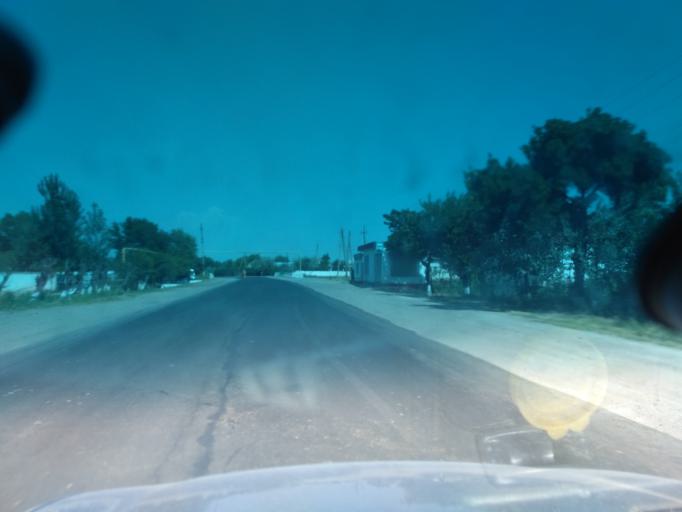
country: UZ
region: Sirdaryo
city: Guliston
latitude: 40.4863
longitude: 68.8986
